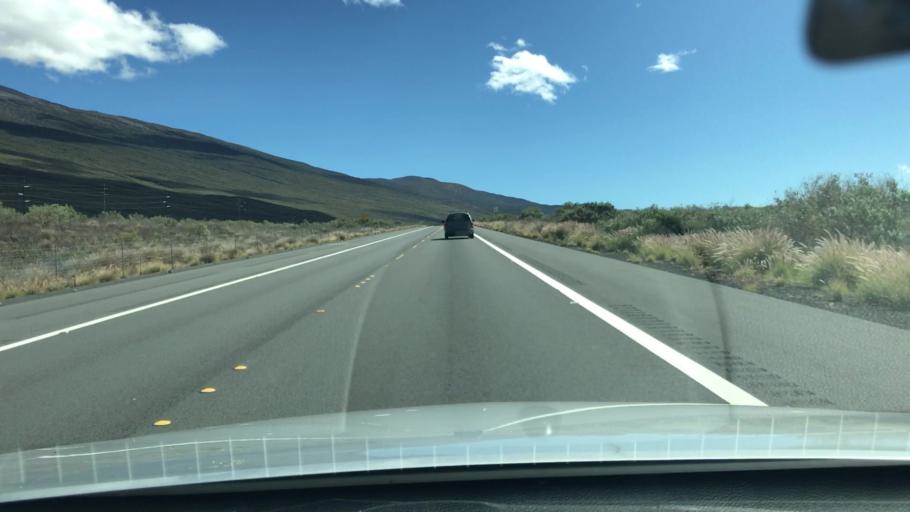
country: US
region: Hawaii
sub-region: Hawaii County
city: Waimea
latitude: 19.7647
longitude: -155.5626
